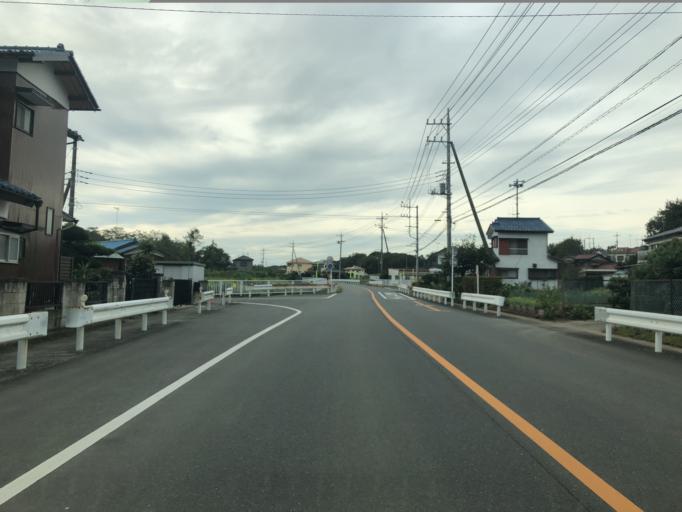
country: JP
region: Saitama
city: Fukiage-fujimi
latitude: 36.0607
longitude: 139.3994
